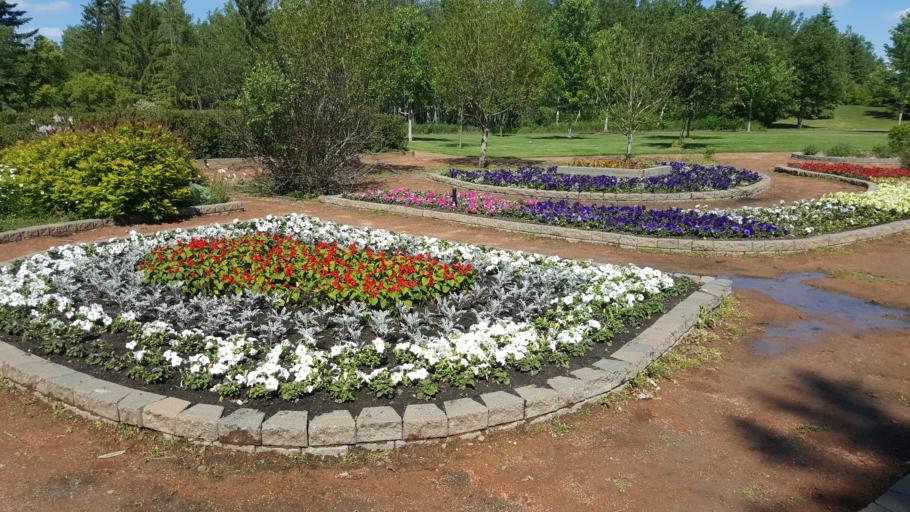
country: CA
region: Saskatchewan
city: Lloydminster
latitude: 53.2617
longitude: -110.0411
